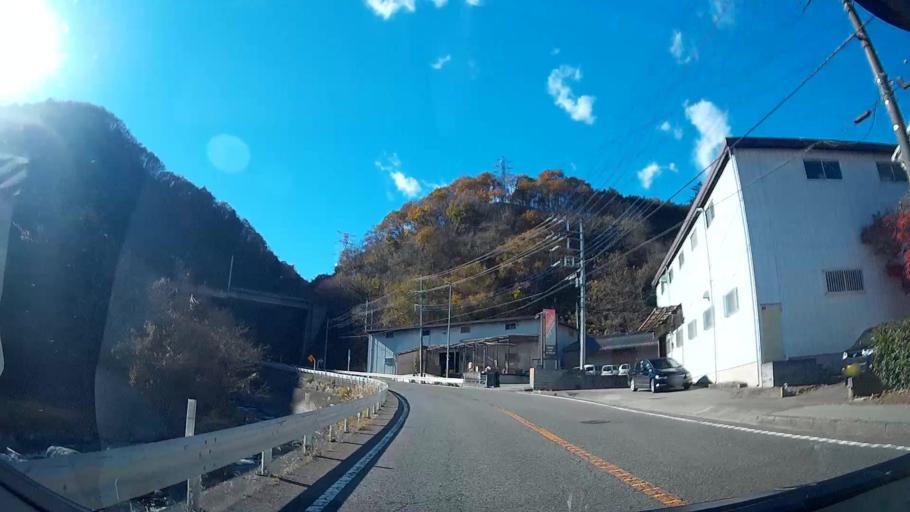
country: JP
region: Yamanashi
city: Otsuki
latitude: 35.6028
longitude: 138.8620
